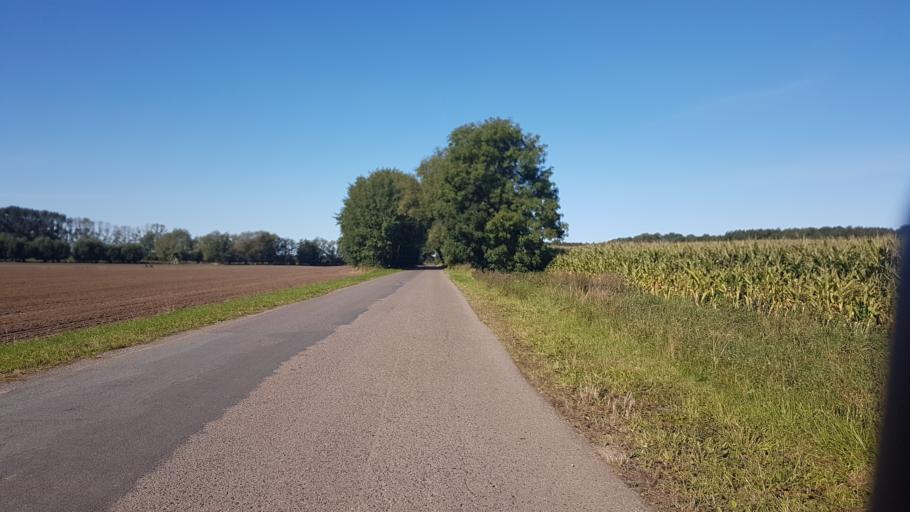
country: DE
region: Mecklenburg-Vorpommern
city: Sagard
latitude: 54.5202
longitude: 13.5264
